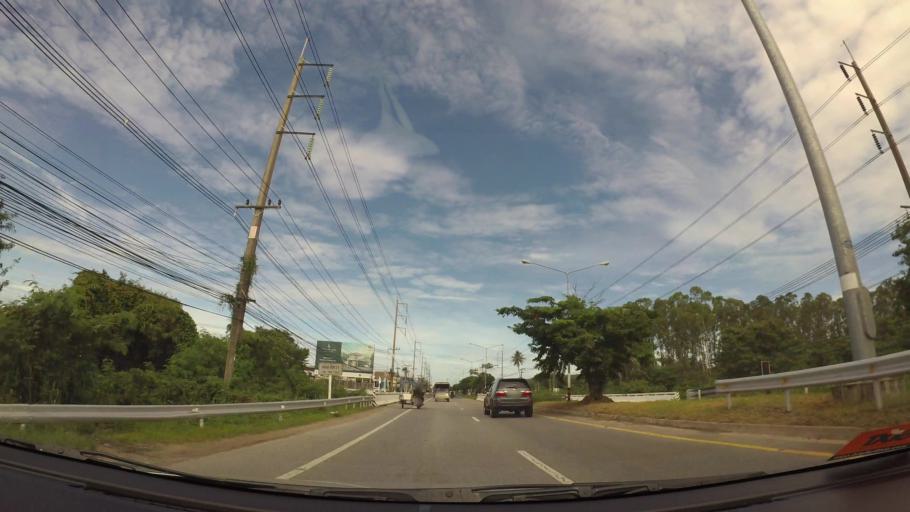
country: TH
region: Rayong
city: Ban Chang
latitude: 12.7322
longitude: 101.0704
